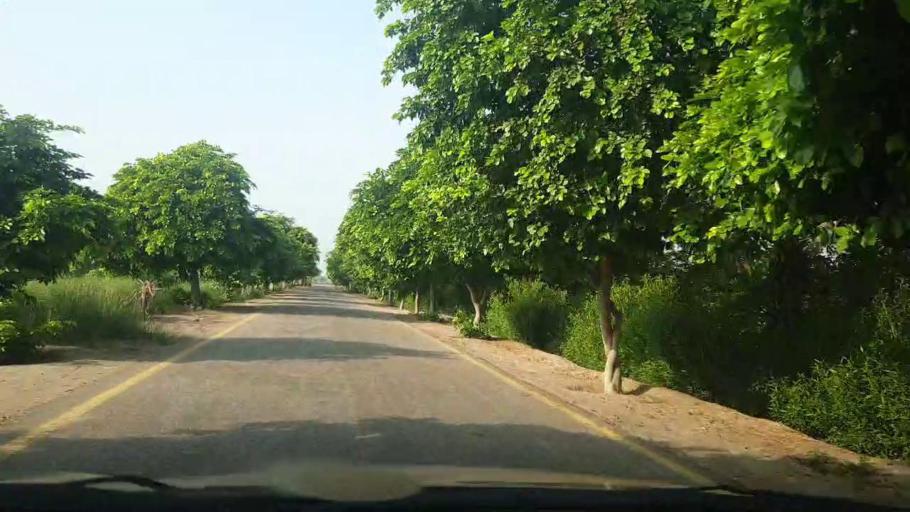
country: PK
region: Sindh
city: Larkana
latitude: 27.5743
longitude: 68.1739
